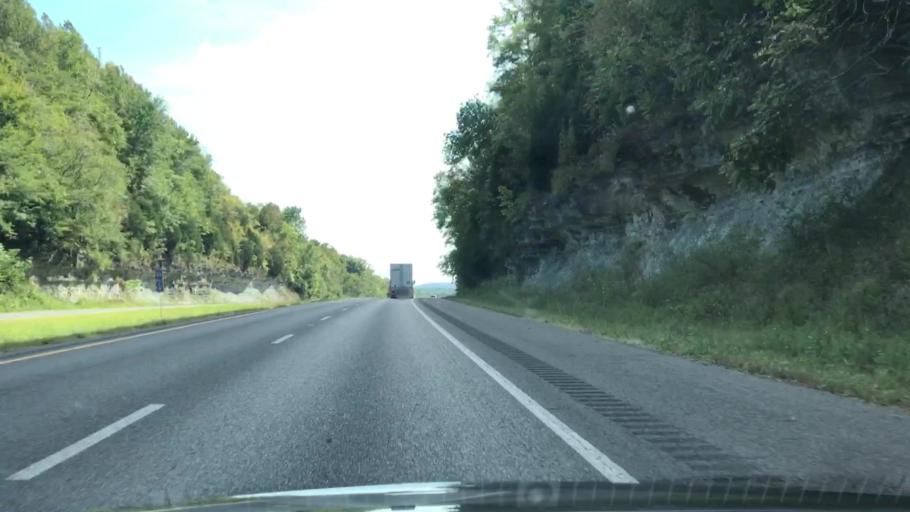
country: US
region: Alabama
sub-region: Limestone County
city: Ardmore
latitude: 35.1194
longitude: -86.8787
